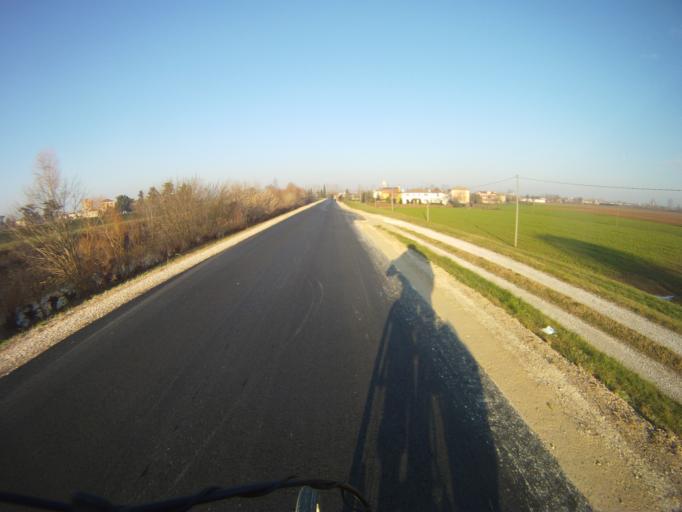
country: IT
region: Veneto
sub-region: Provincia di Padova
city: Legnaro
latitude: 45.3399
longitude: 11.9389
